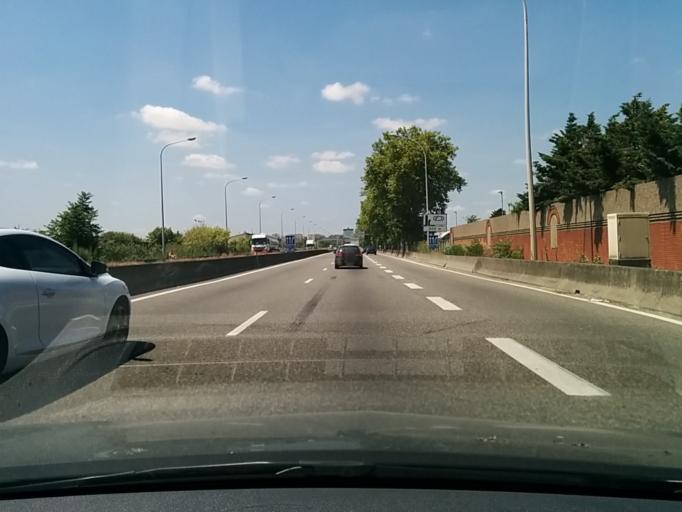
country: FR
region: Midi-Pyrenees
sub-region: Departement de la Haute-Garonne
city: Colomiers
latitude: 43.6091
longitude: 1.3649
